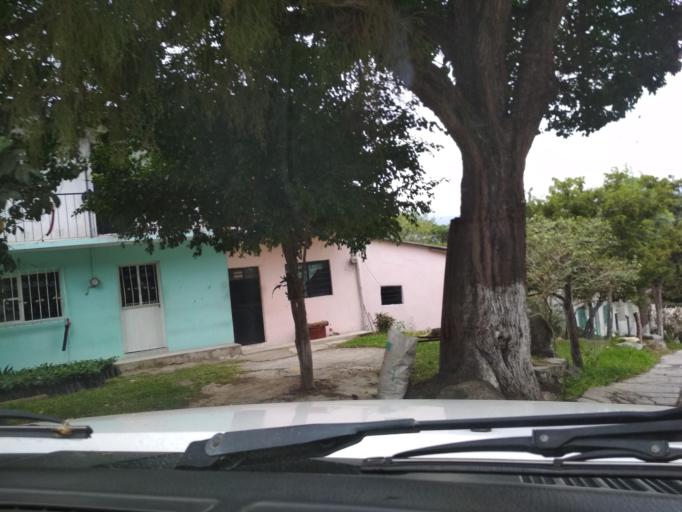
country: MX
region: Veracruz
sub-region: Actopan
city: Trapiche del Rosario
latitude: 19.5613
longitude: -96.7938
